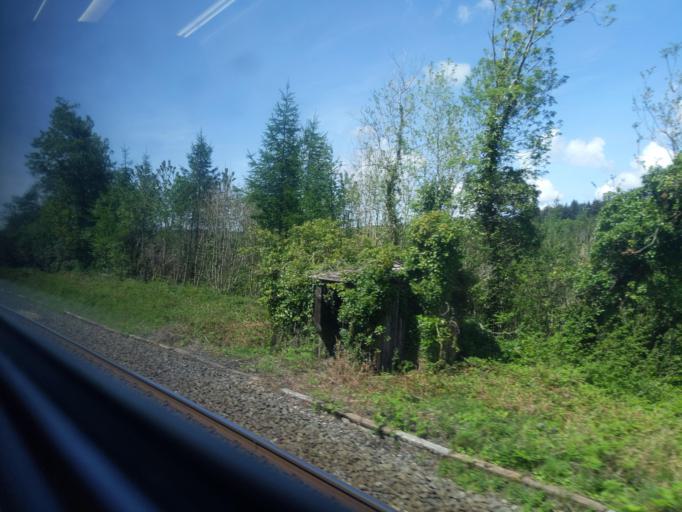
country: GB
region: England
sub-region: Cornwall
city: Lostwithiel
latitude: 50.4543
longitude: -4.5850
